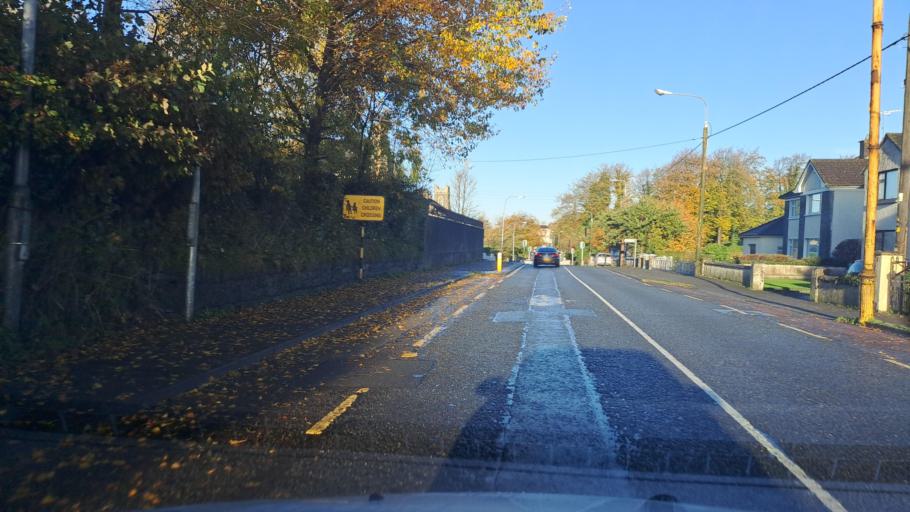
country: IE
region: Ulster
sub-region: An Cabhan
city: Cootehill
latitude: 54.0729
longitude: -7.0738
